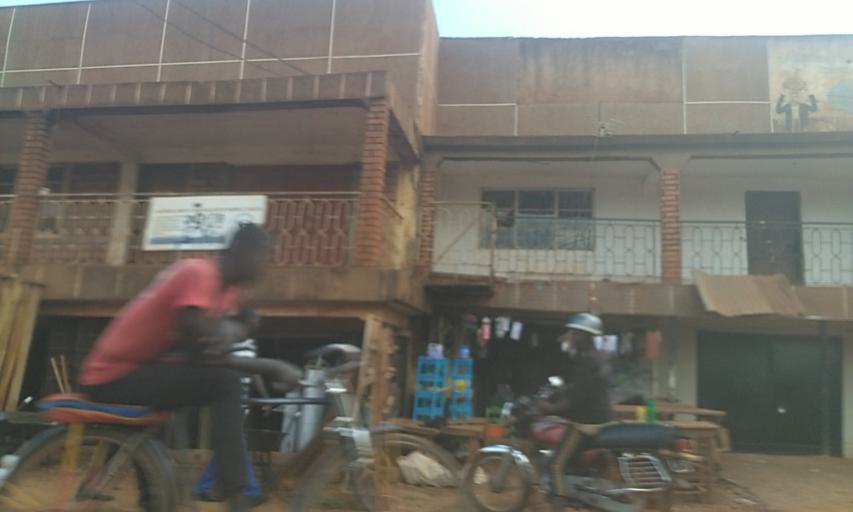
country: UG
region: Central Region
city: Kampala Central Division
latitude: 0.2992
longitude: 32.5320
